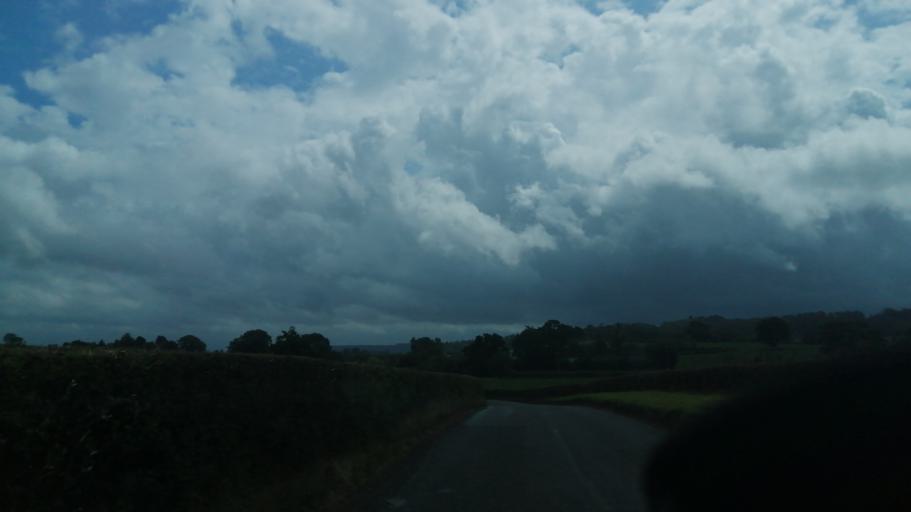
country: GB
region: England
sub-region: Herefordshire
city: Kingstone
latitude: 52.0110
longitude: -2.8328
